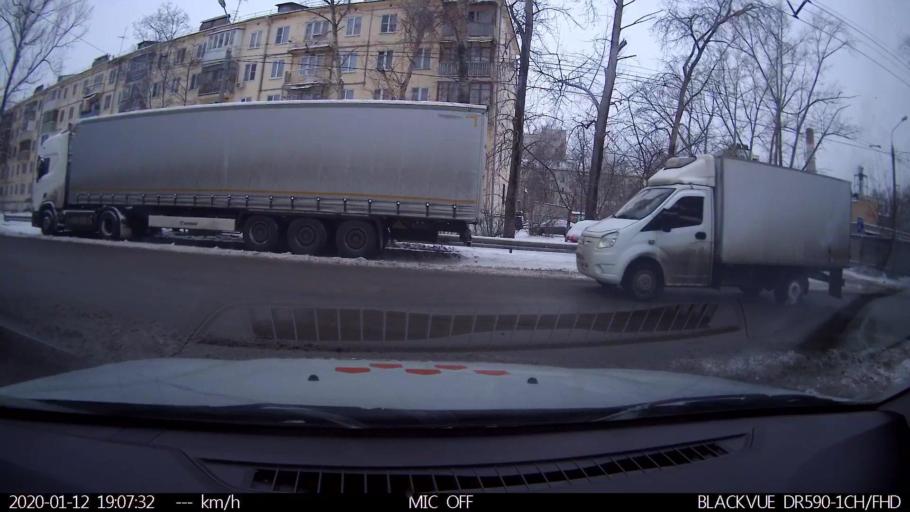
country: RU
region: Nizjnij Novgorod
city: Nizhniy Novgorod
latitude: 56.3307
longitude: 43.9142
